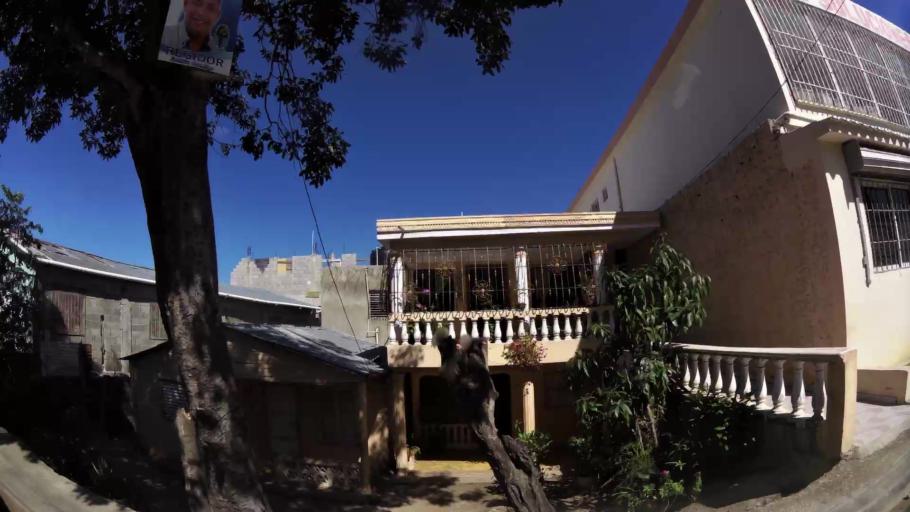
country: DO
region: San Cristobal
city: San Cristobal
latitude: 18.4303
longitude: -70.1323
